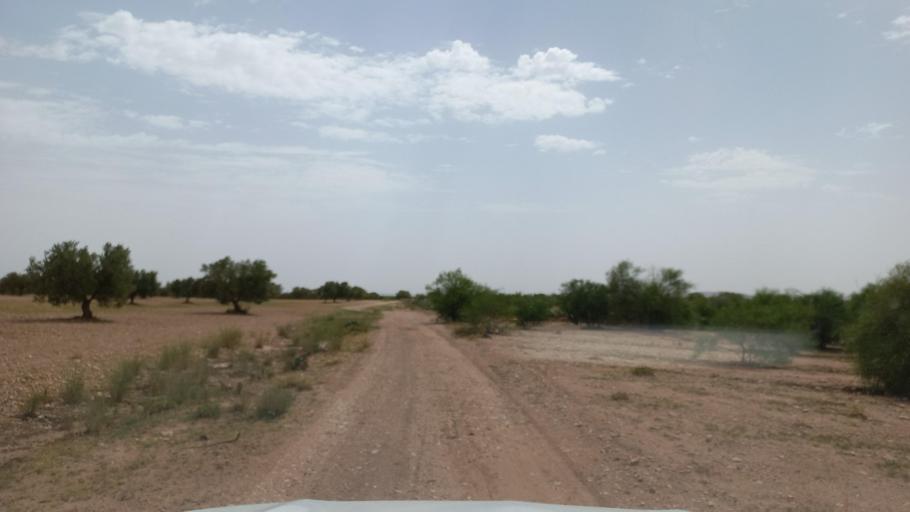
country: TN
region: Al Qasrayn
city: Kasserine
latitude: 35.2938
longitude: 9.0187
